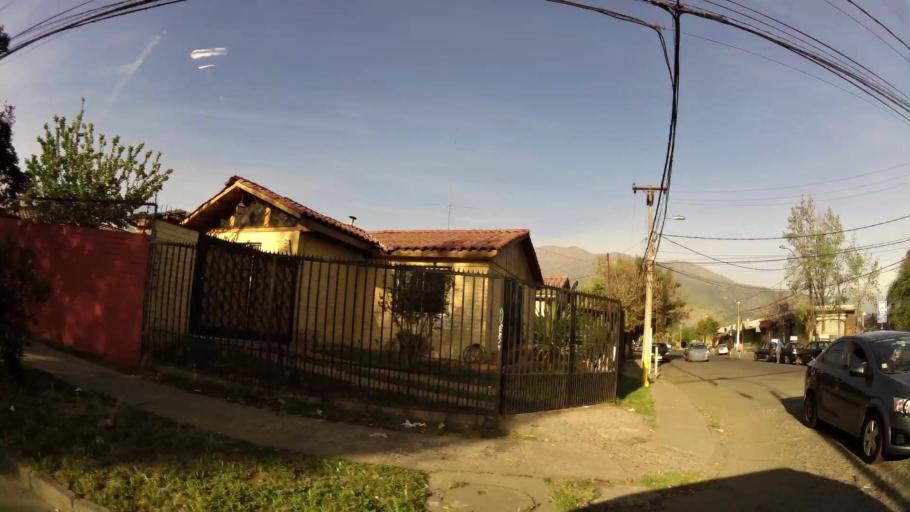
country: CL
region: Santiago Metropolitan
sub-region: Provincia de Cordillera
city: Puente Alto
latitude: -33.5415
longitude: -70.5706
